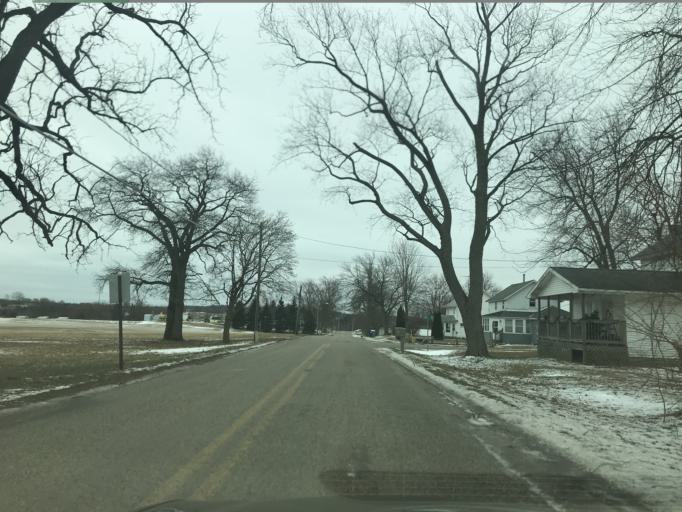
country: US
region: Michigan
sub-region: Jackson County
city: Brooklyn
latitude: 42.0674
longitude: -84.3260
